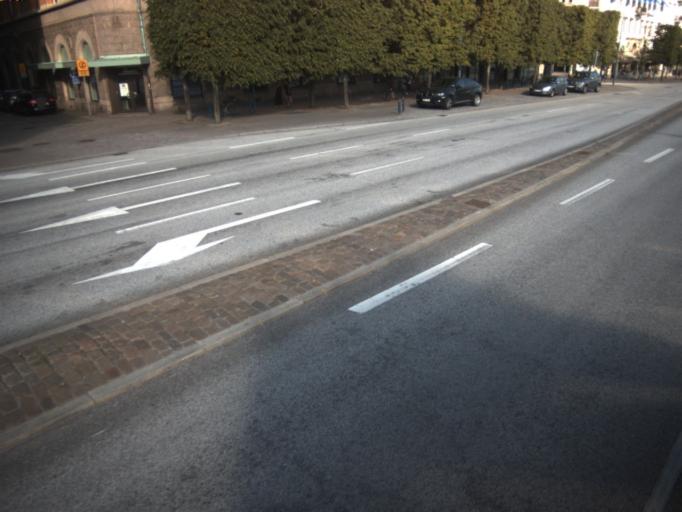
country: SE
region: Skane
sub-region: Helsingborg
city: Helsingborg
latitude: 56.0458
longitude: 12.6931
